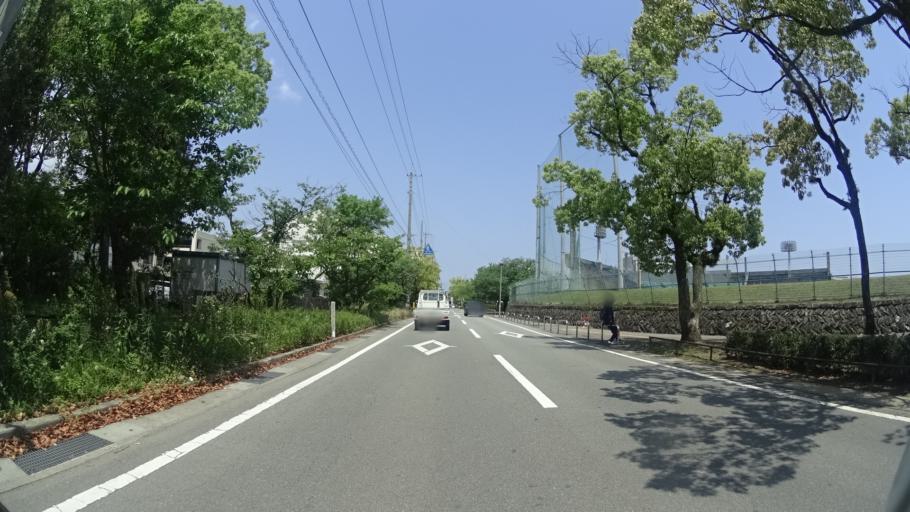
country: JP
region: Tokushima
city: Tokushima-shi
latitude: 34.0730
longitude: 134.5131
